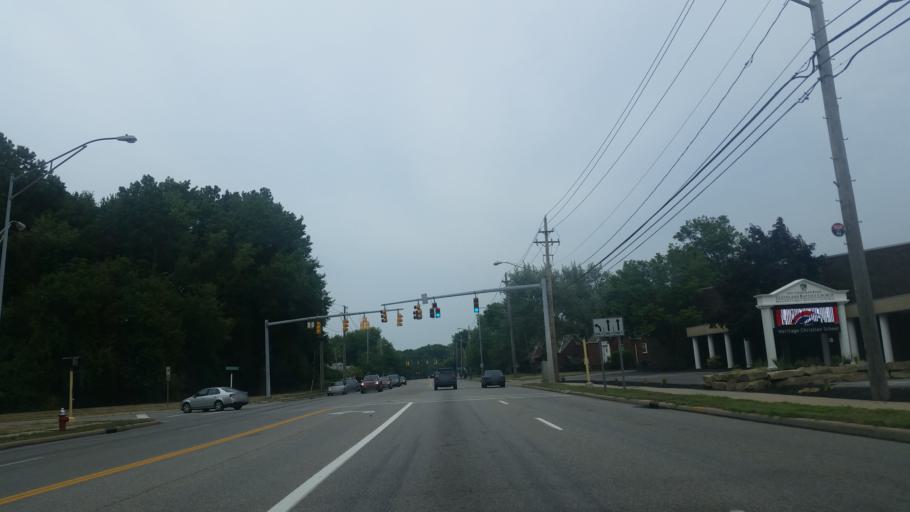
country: US
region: Ohio
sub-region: Cuyahoga County
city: Brooklyn
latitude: 41.4367
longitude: -81.7583
